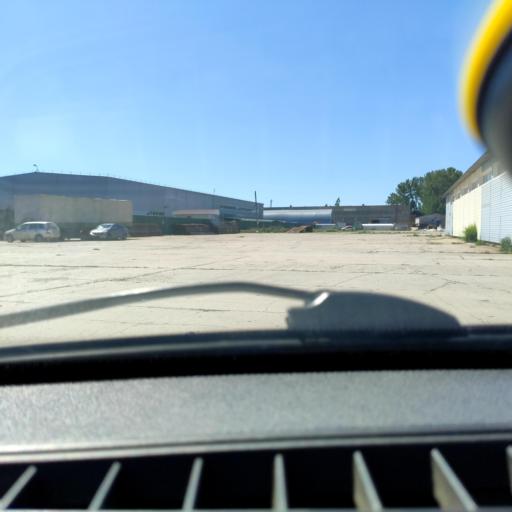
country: RU
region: Samara
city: Tol'yatti
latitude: 53.5733
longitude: 49.3023
